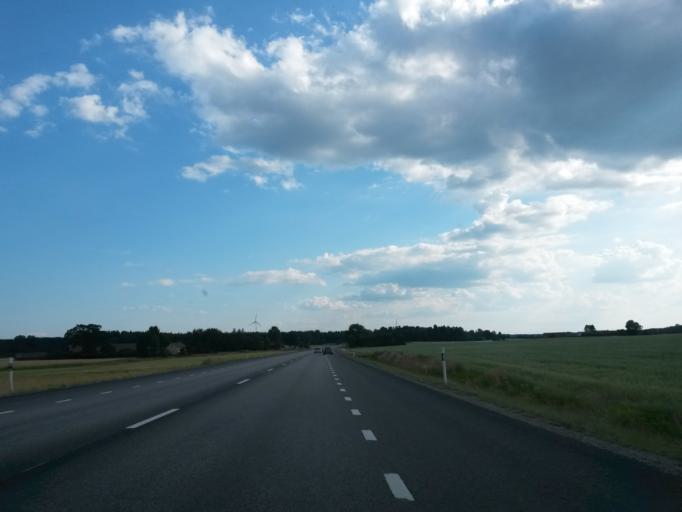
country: SE
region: Vaestra Goetaland
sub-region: Vargarda Kommun
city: Vargarda
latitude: 58.1373
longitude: 12.8612
